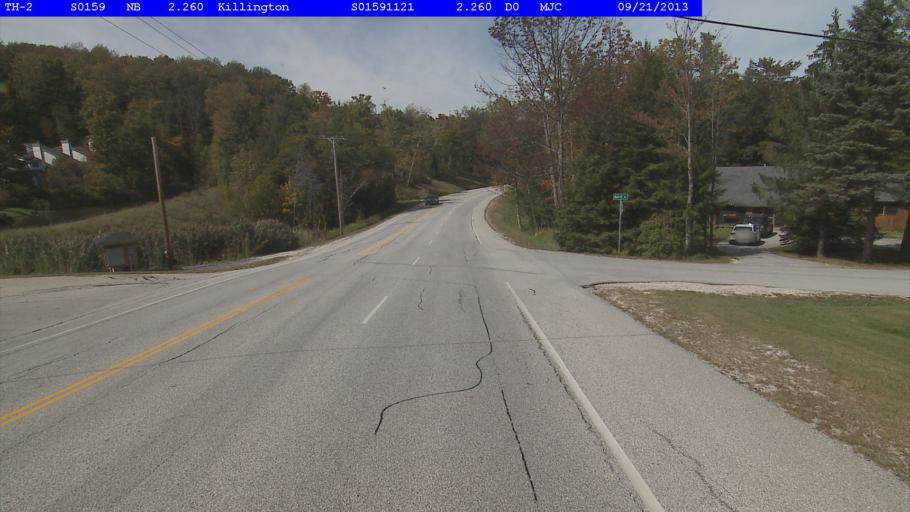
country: US
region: Vermont
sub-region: Rutland County
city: Rutland
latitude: 43.6595
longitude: -72.7953
